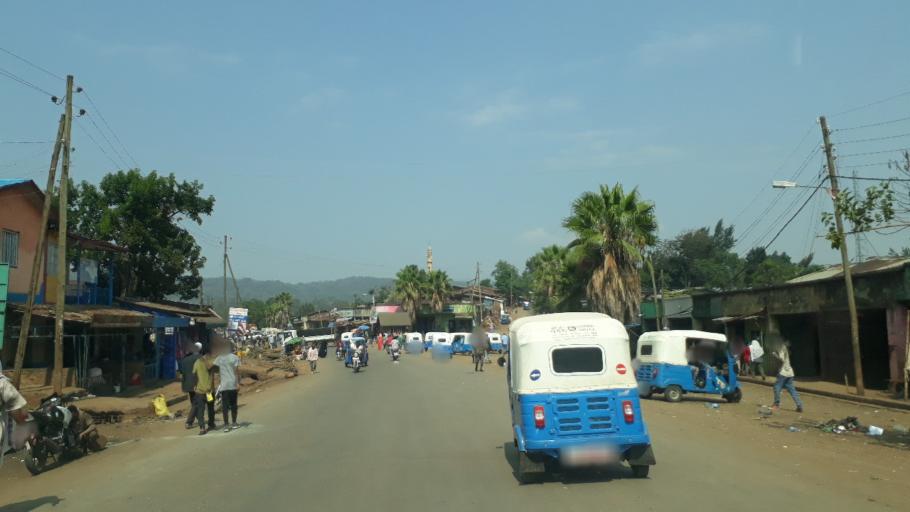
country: ET
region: Oromiya
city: Agaro
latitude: 7.8581
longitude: 36.5822
